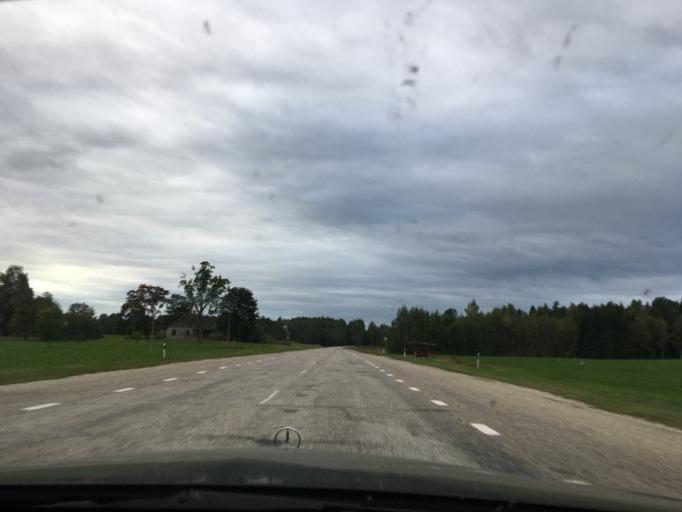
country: LV
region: Aluksnes Rajons
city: Aluksne
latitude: 57.6093
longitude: 27.2539
